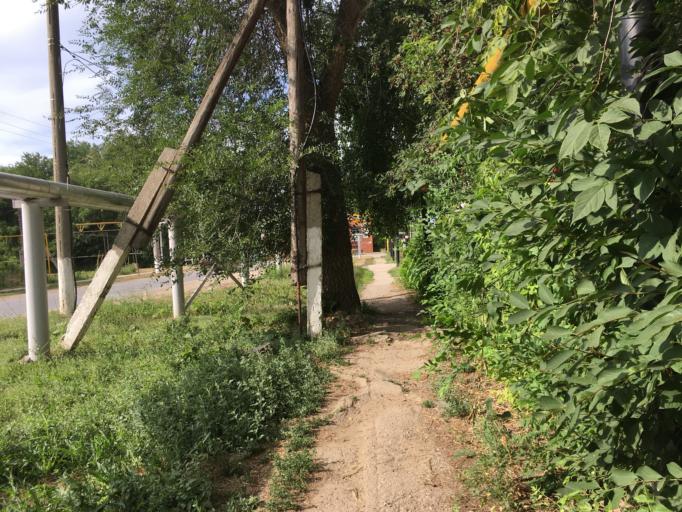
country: RU
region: Samara
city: Bezenchuk
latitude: 52.9877
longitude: 49.4410
